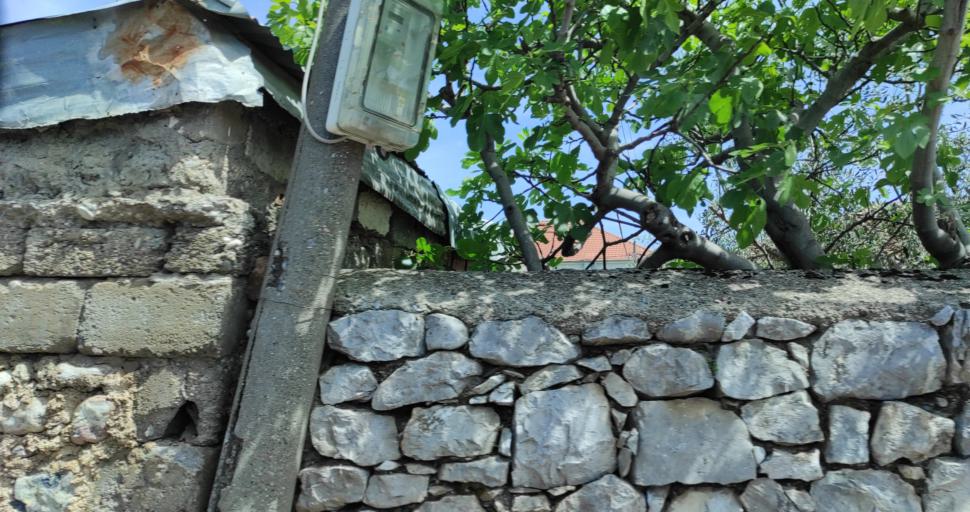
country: AL
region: Shkoder
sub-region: Rrethi i Malesia e Madhe
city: Gruemire
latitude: 42.1289
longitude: 19.5535
